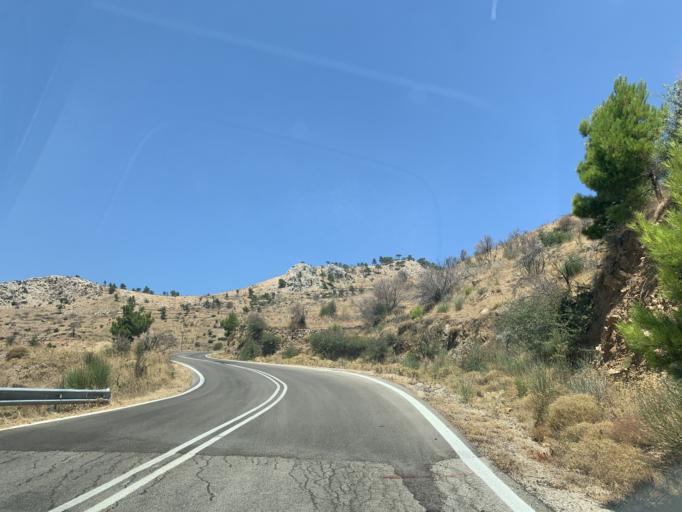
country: GR
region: North Aegean
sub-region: Chios
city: Vrontados
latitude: 38.4516
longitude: 25.9777
